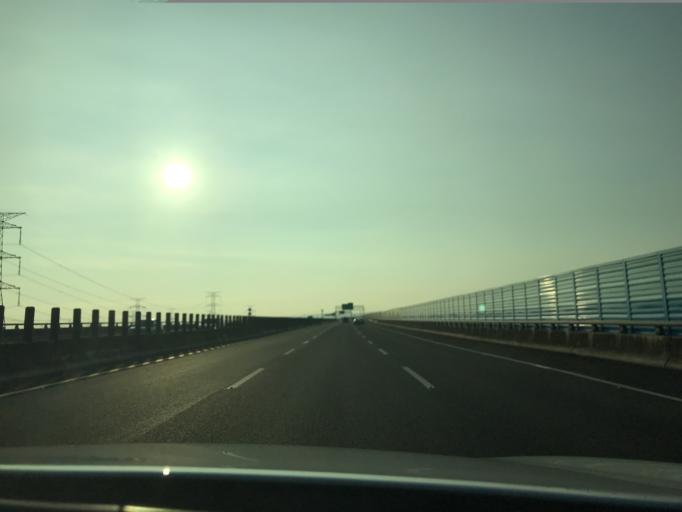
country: TW
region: Taiwan
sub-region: Changhua
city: Chang-hua
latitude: 24.1171
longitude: 120.5390
